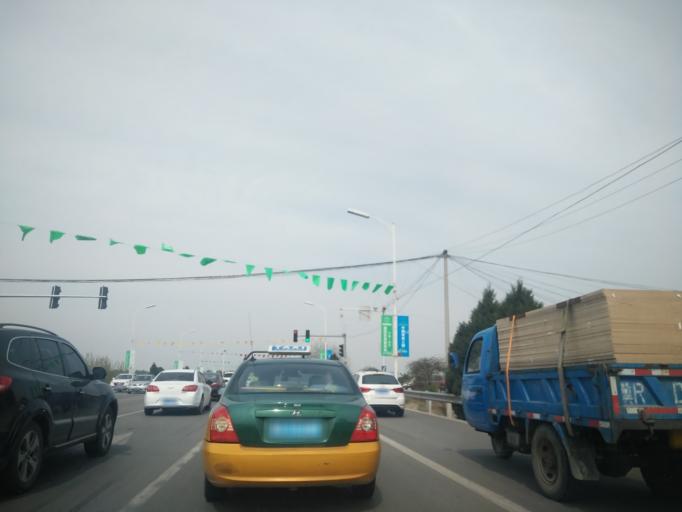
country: CN
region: Beijing
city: Xiji
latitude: 39.7772
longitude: 116.9806
